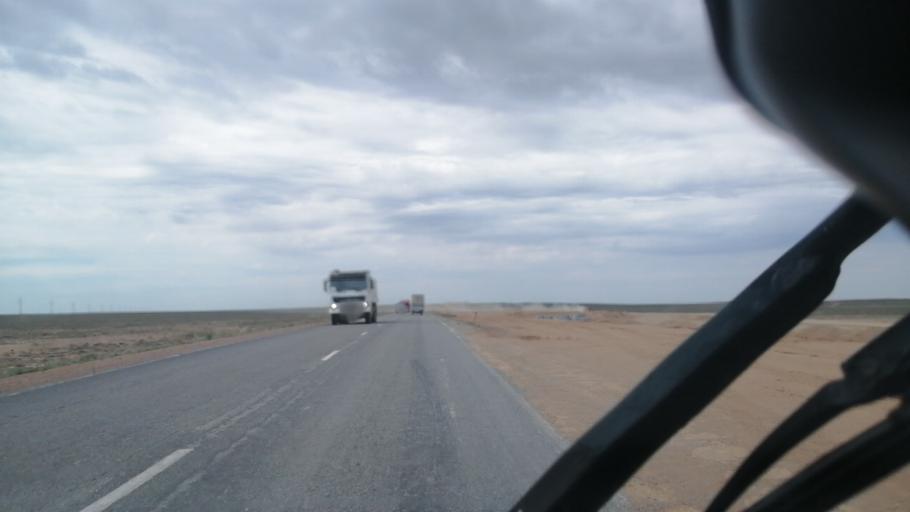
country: KZ
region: Qaraghandy
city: Saryshaghan
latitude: 46.5112
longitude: 74.1045
